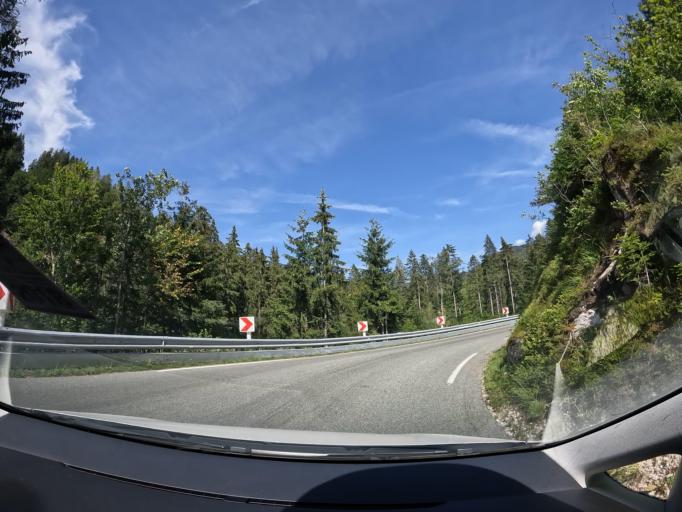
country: AT
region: Carinthia
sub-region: Politischer Bezirk Klagenfurt Land
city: Schiefling am See
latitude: 46.6075
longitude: 14.1059
